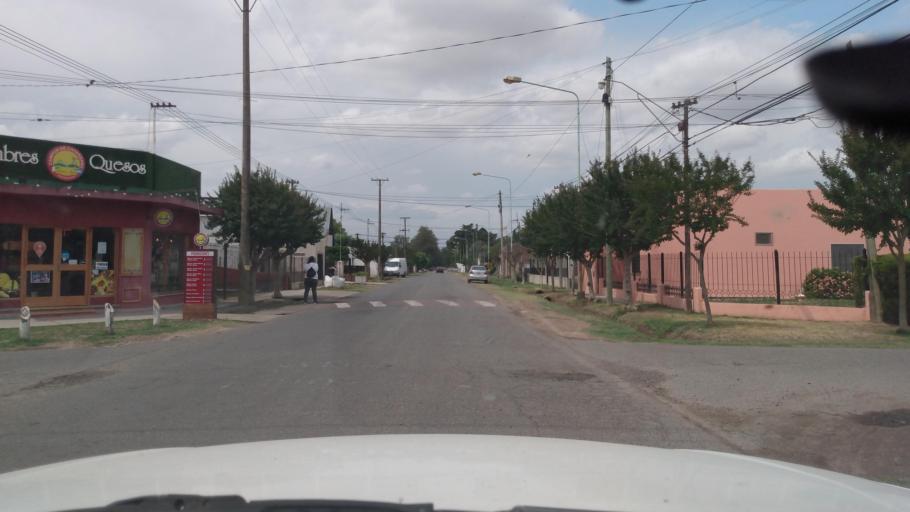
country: AR
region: Buenos Aires
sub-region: Partido de Lujan
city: Lujan
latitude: -34.5565
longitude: -59.2024
